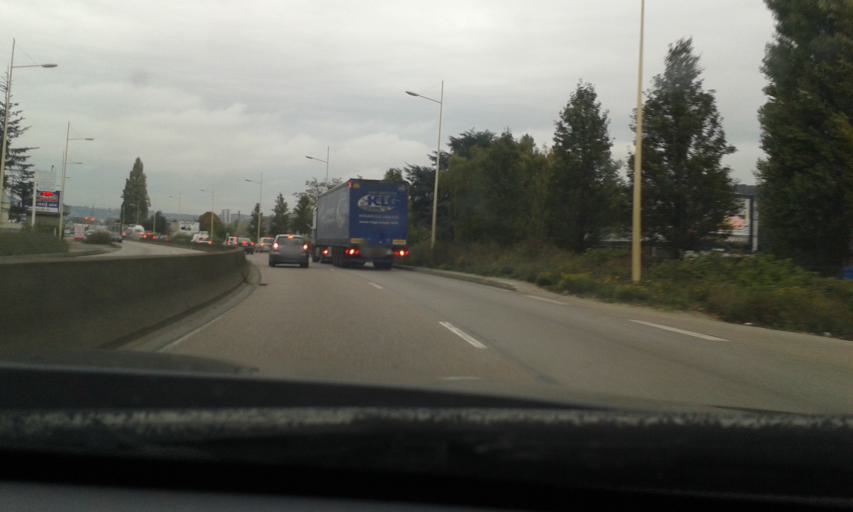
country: FR
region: Haute-Normandie
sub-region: Departement de la Seine-Maritime
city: Sotteville-les-Rouen
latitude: 49.4178
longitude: 1.1083
